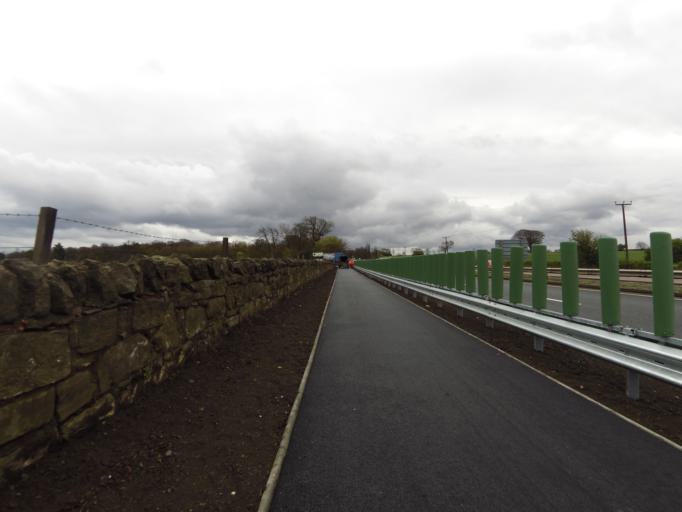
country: GB
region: Scotland
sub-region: Edinburgh
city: Queensferry
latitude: 55.9767
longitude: -3.3399
